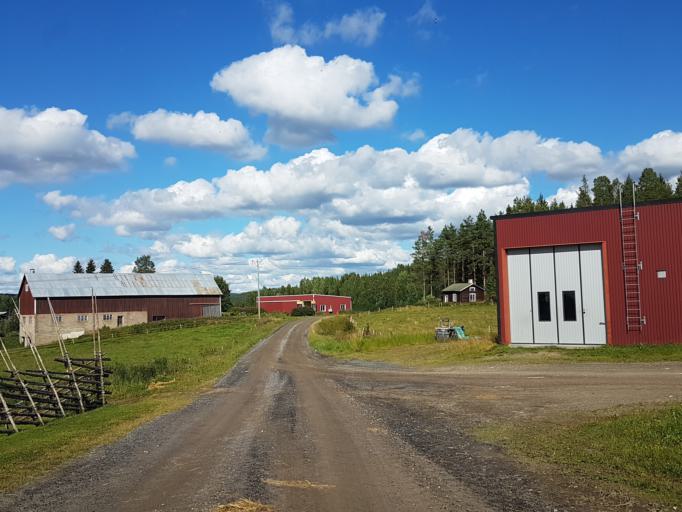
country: SE
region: Vaesterbotten
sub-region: Skelleftea Kommun
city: Burtraesk
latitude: 64.2968
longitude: 20.4859
